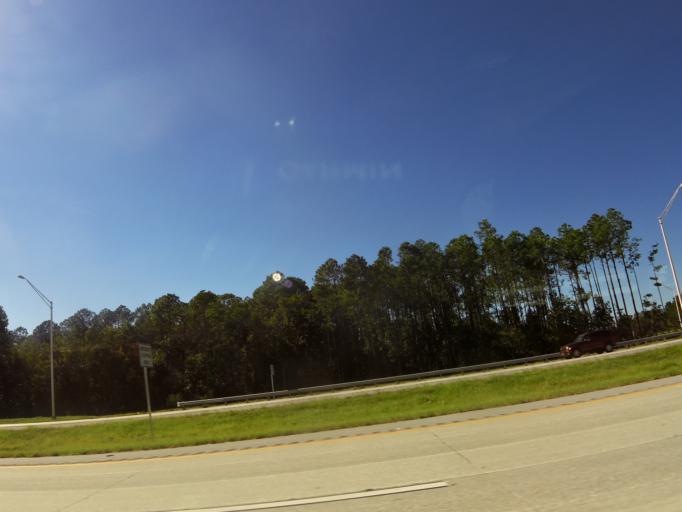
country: US
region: Florida
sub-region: Saint Johns County
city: Palm Valley
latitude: 30.1299
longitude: -81.5103
